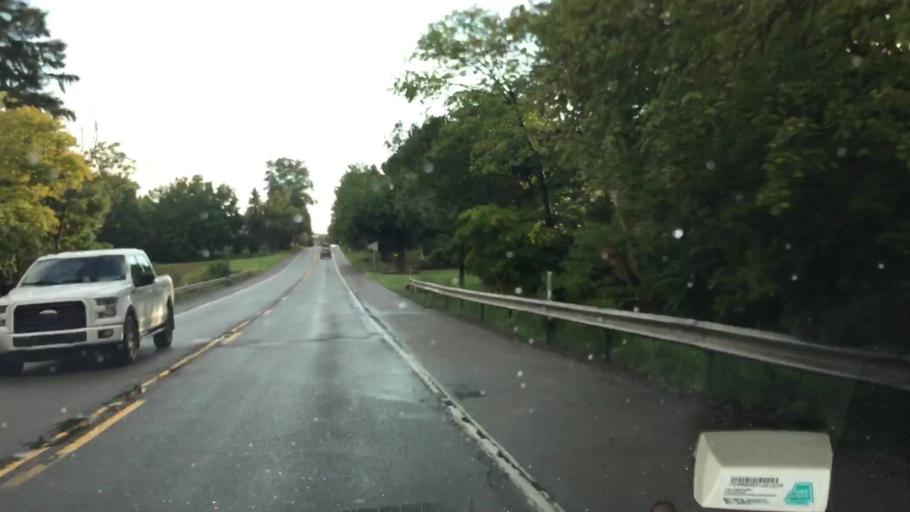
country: US
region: Pennsylvania
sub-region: Butler County
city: Meridian
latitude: 40.8654
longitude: -79.9590
